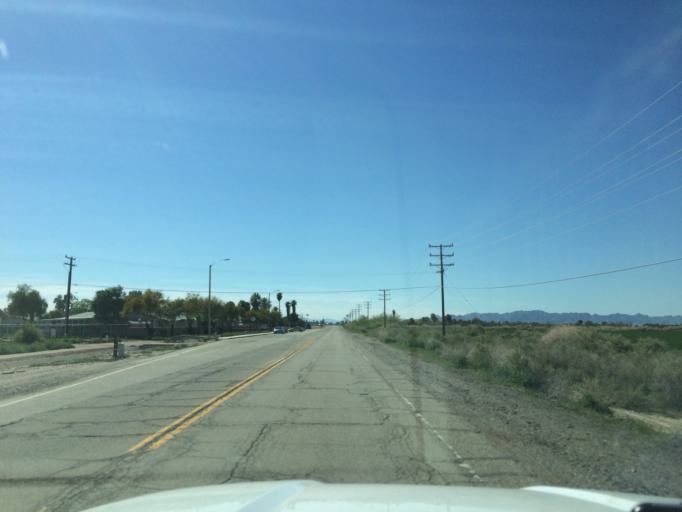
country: US
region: Arizona
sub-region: La Paz County
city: Ehrenberg
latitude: 33.6110
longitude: -114.5569
